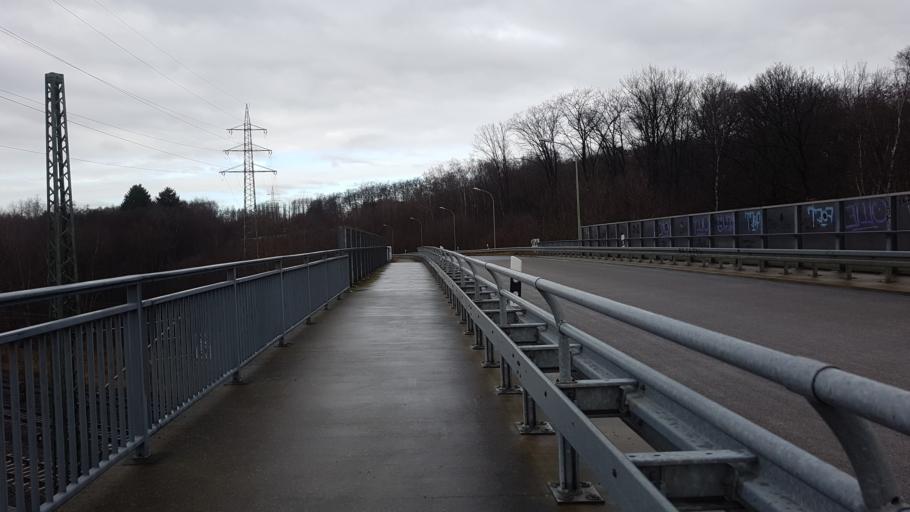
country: DE
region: North Rhine-Westphalia
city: Stolberg
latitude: 50.7932
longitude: 6.2138
